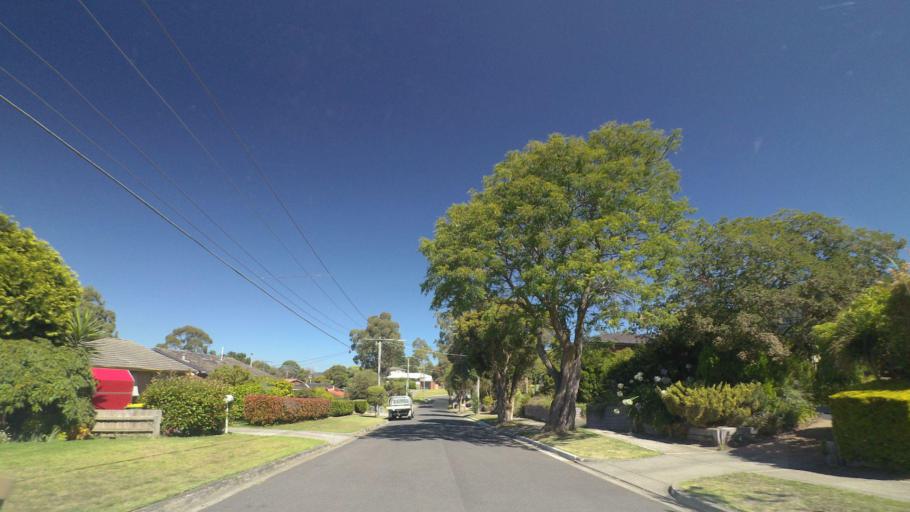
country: AU
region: Victoria
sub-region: Yarra Ranges
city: Chirnside Park
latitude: -37.7463
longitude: 145.3253
